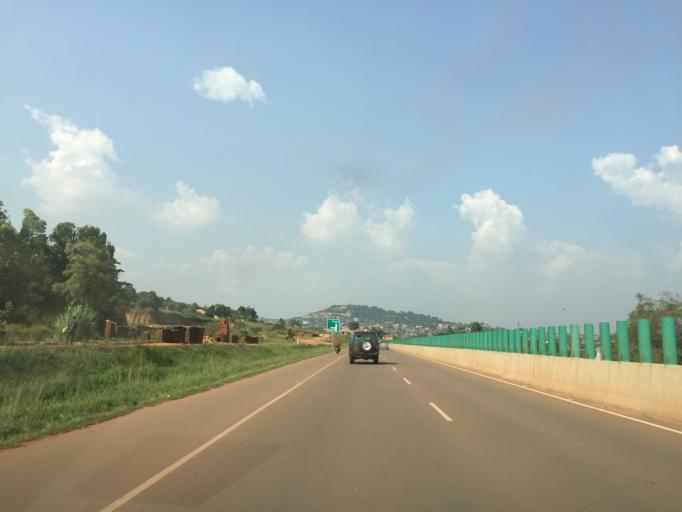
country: UG
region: Central Region
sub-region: Wakiso District
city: Kajansi
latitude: 0.2305
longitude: 32.6068
